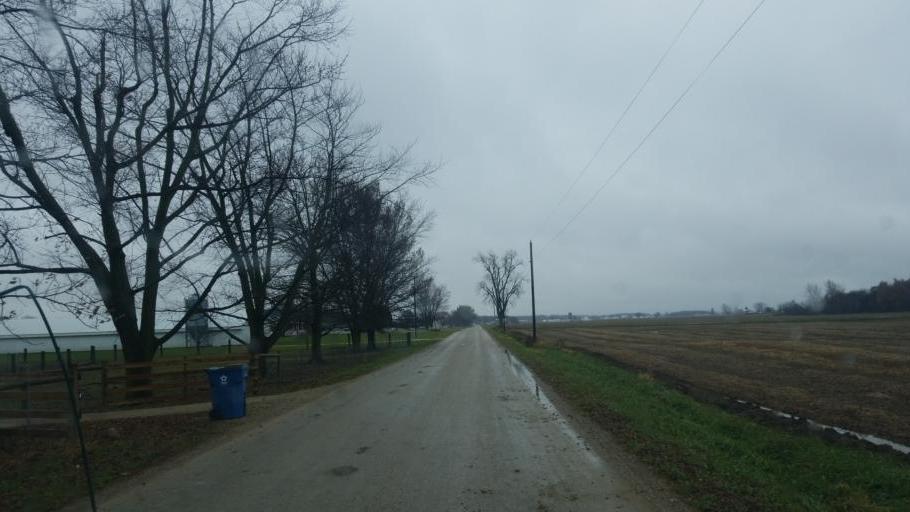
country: US
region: Indiana
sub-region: Adams County
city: Berne
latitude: 40.6675
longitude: -84.9173
